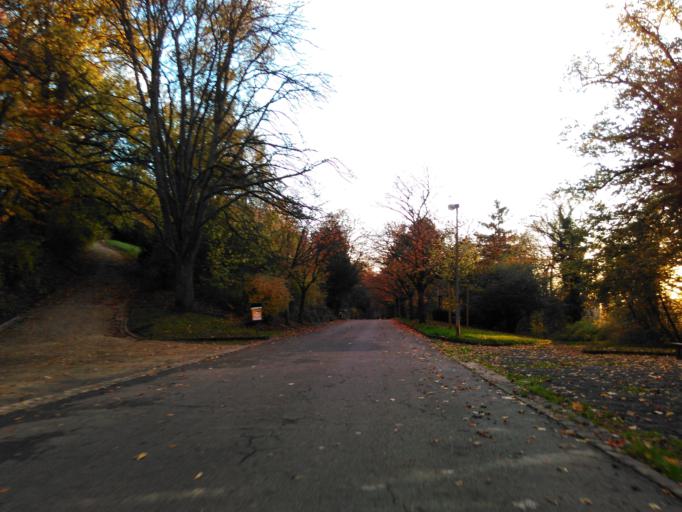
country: LU
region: Luxembourg
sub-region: Canton d'Esch-sur-Alzette
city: Esch-sur-Alzette
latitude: 49.4946
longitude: 5.9880
